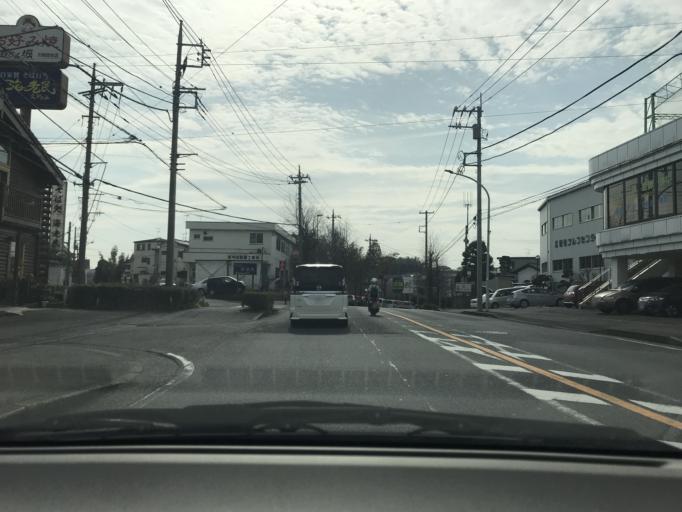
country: JP
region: Tokyo
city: Chofugaoka
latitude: 35.5980
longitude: 139.5549
